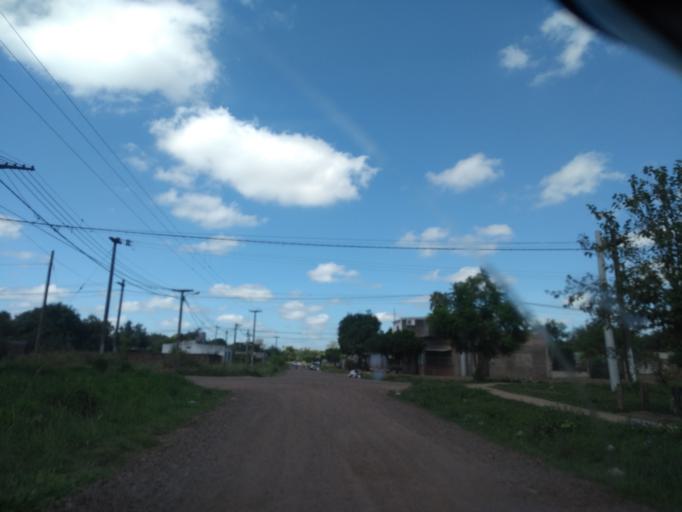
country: AR
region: Chaco
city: Fontana
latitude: -27.4076
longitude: -59.0425
